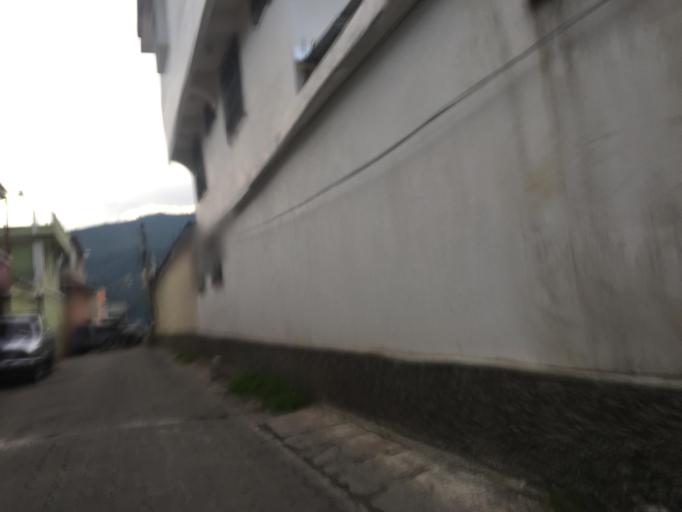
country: GT
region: Totonicapan
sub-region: Municipio de Totonicapan
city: Totonicapan
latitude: 14.9090
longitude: -91.3631
